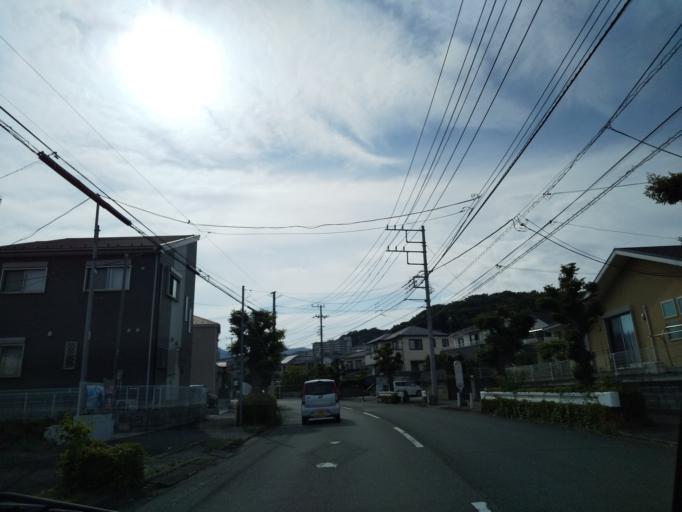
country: JP
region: Kanagawa
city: Zama
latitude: 35.4915
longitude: 139.3343
